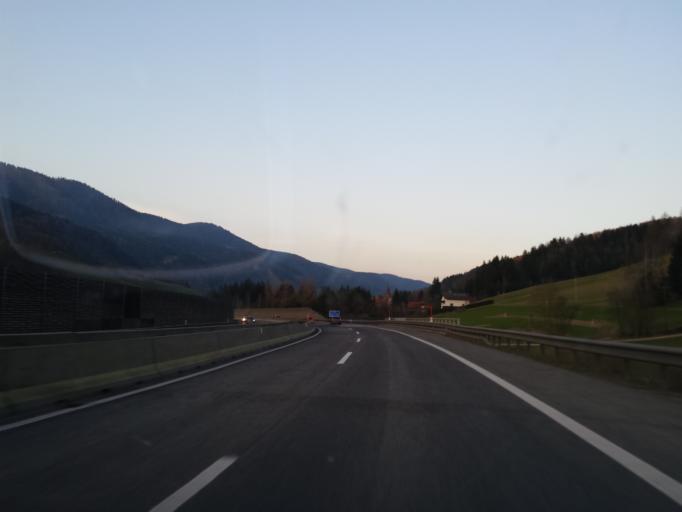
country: AT
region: Styria
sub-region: Politischer Bezirk Bruck-Muerzzuschlag
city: Spital am Semmering
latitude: 47.6015
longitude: 15.7293
